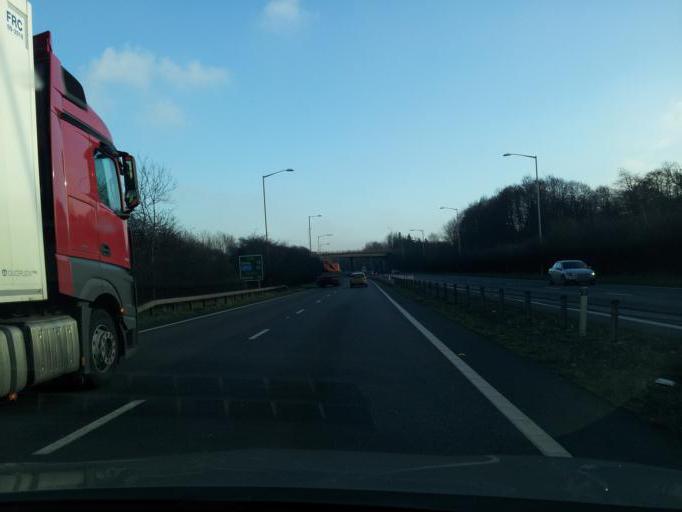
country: GB
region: England
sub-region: Staffordshire
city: Uttoxeter
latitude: 52.9117
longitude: -1.8913
